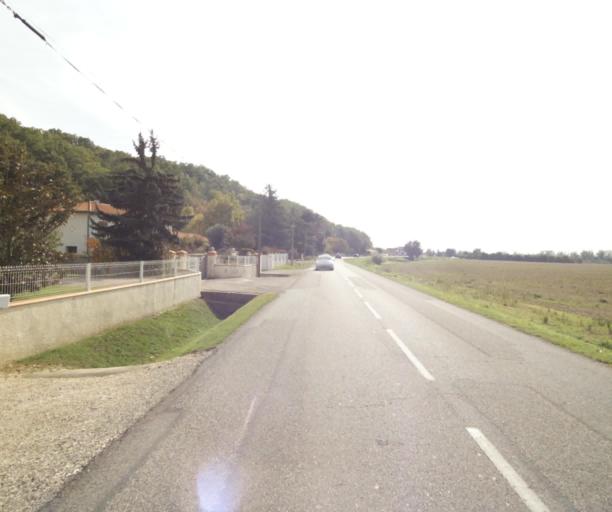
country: FR
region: Midi-Pyrenees
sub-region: Departement du Tarn-et-Garonne
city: Corbarieu
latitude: 43.9551
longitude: 1.3644
